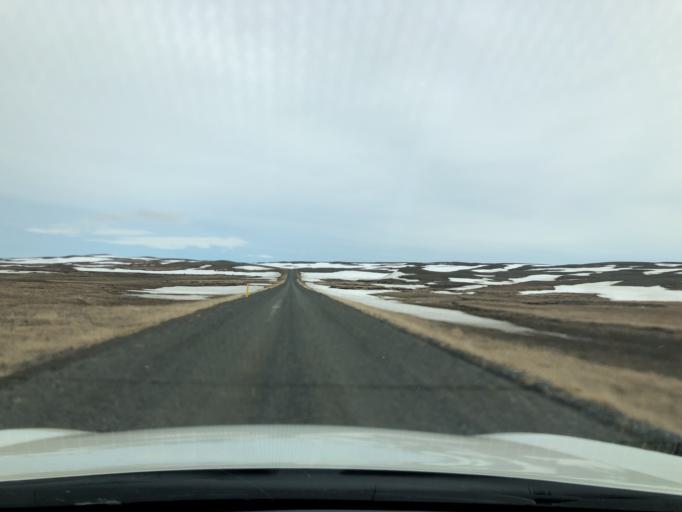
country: IS
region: East
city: Egilsstadir
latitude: 65.3006
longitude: -15.4118
